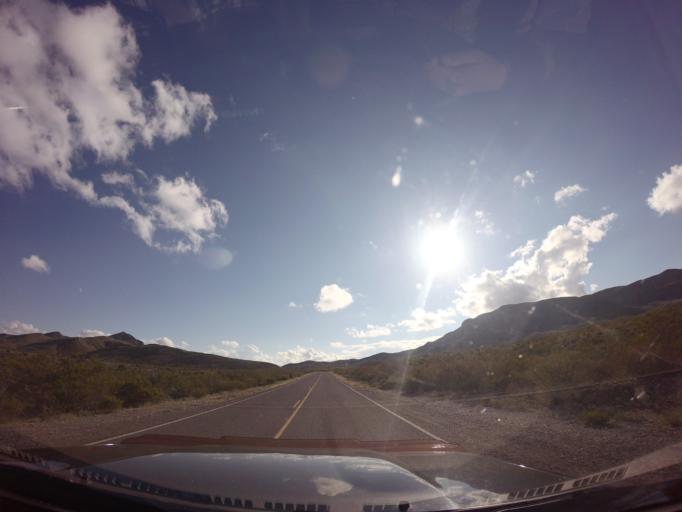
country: US
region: Texas
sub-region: Brewster County
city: Alpine
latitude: 29.6792
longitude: -103.1677
